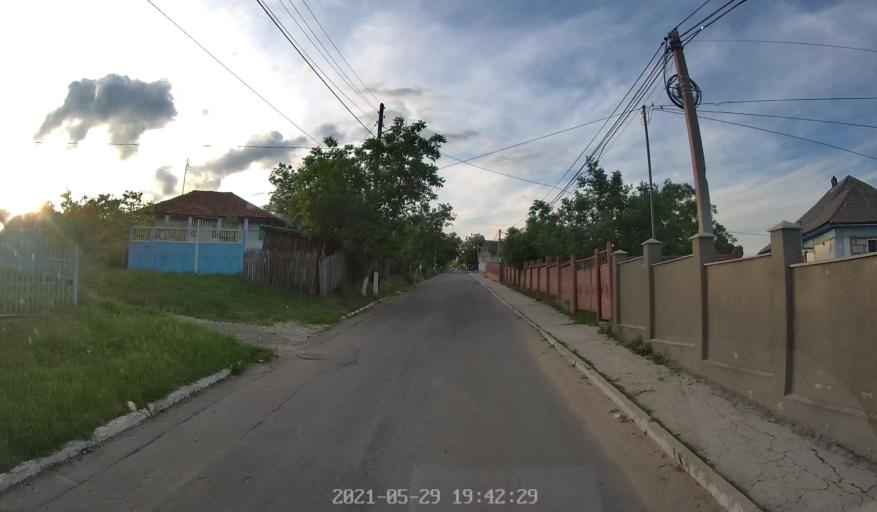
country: MD
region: Chisinau
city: Singera
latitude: 46.8288
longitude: 28.9737
